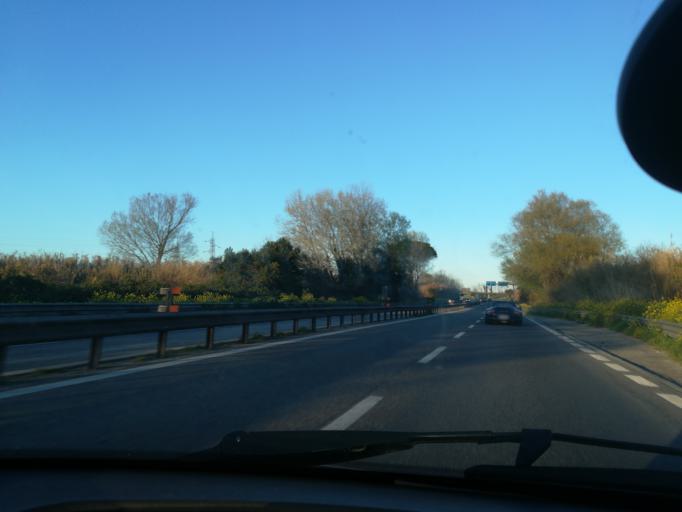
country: IT
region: The Marches
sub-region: Provincia di Macerata
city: Santa Maria Apparente
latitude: 43.2866
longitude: 13.7036
